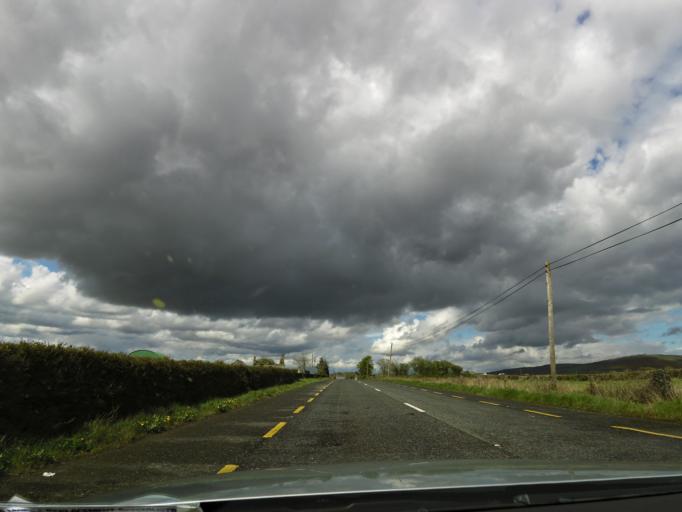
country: IE
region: Leinster
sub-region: Laois
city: Rathdowney
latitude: 52.7718
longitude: -7.5389
